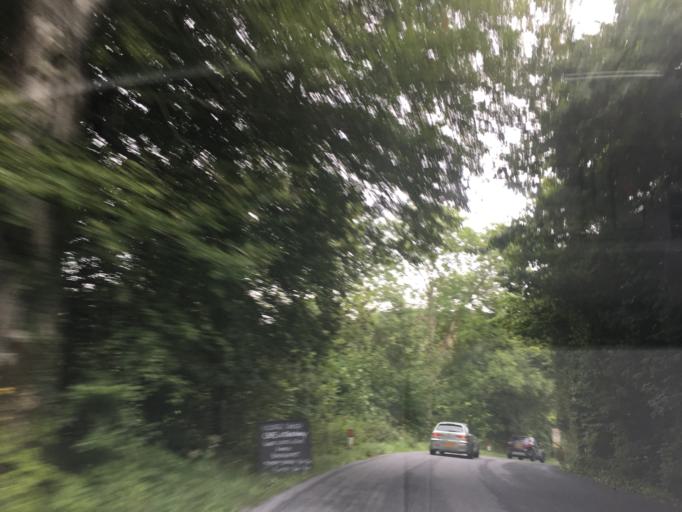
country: GB
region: Scotland
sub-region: Argyll and Bute
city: Oban
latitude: 56.2642
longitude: -5.4752
